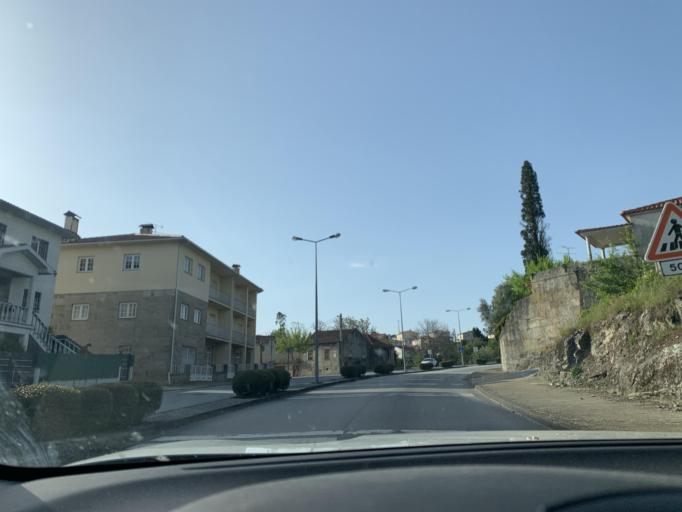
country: PT
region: Viseu
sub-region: Mangualde
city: Mangualde
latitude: 40.5870
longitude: -7.7642
